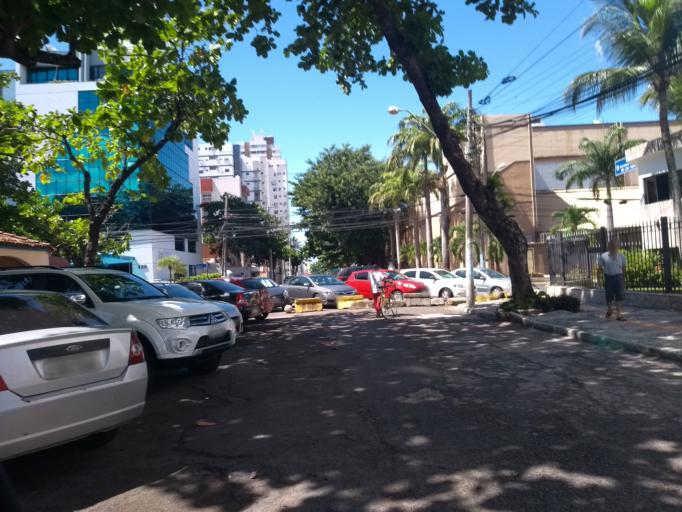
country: BR
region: Bahia
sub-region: Salvador
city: Salvador
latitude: -13.0010
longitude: -38.4575
